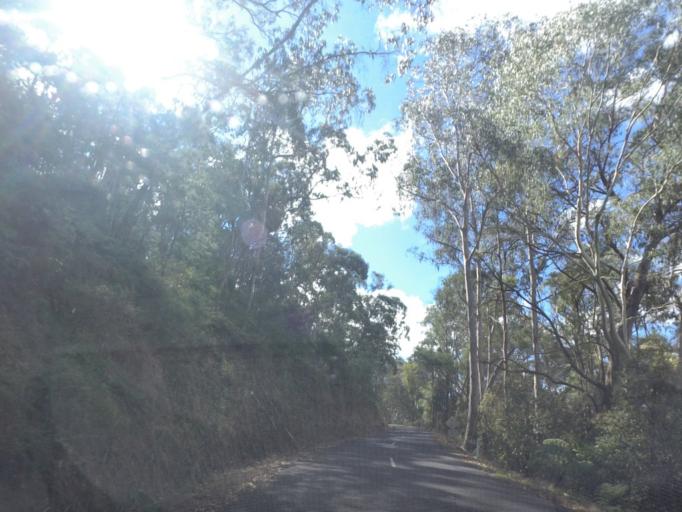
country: AU
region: Victoria
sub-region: Murrindindi
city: Alexandra
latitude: -37.3385
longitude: 145.9540
